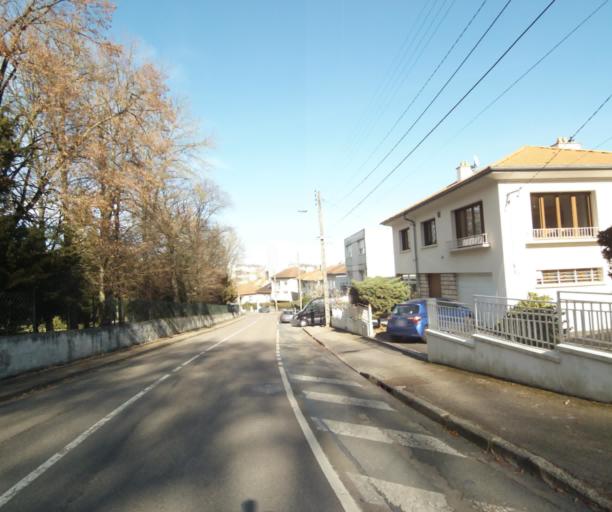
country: FR
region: Lorraine
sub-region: Departement de Meurthe-et-Moselle
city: Villers-les-Nancy
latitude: 48.6744
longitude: 6.1451
